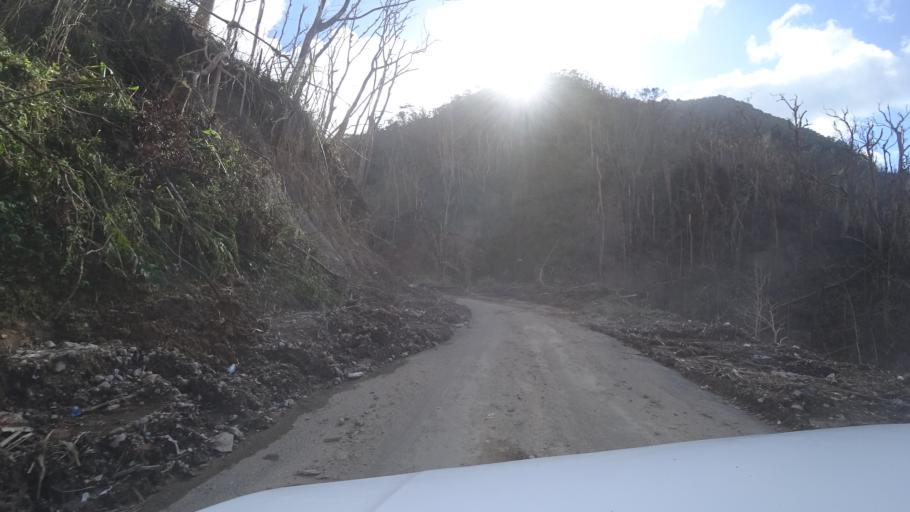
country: DM
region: Saint Luke
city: Pointe Michel
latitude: 15.2651
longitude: -61.3490
